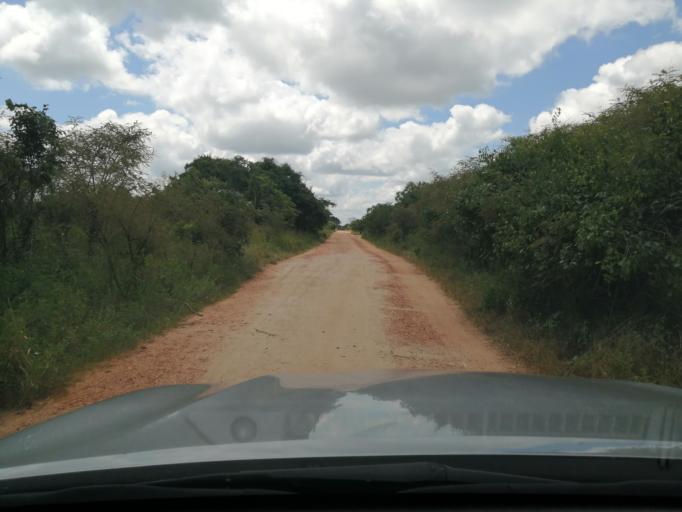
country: ZM
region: Lusaka
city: Lusaka
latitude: -15.1323
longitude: 27.9015
